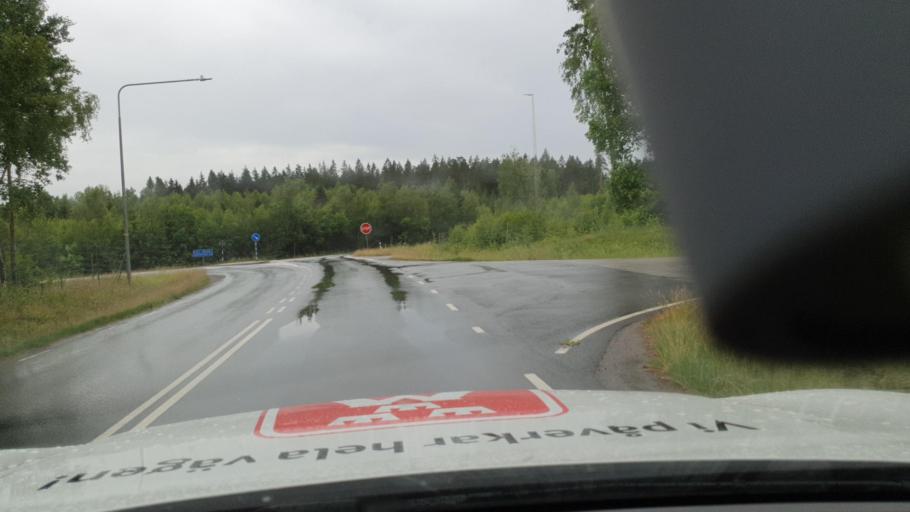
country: SE
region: Vaestra Goetaland
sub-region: Mariestads Kommun
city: Mariestad
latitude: 58.7283
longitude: 13.8922
